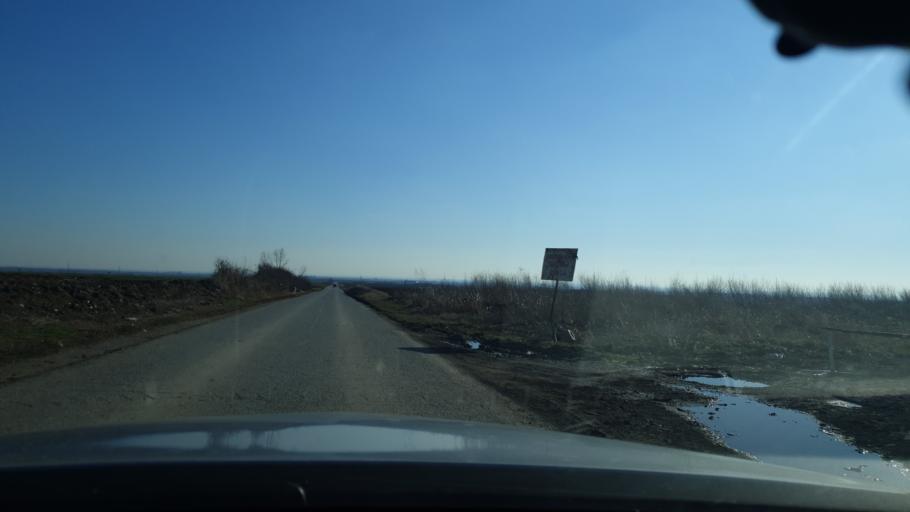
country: RS
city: Vrdnik
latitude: 45.0885
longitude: 19.8064
